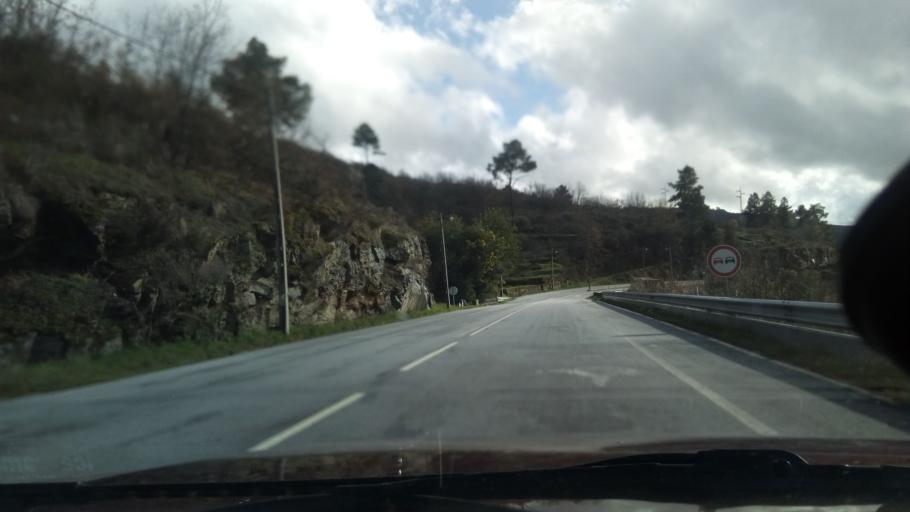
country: PT
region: Guarda
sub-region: Guarda
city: Guarda
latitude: 40.5712
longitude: -7.2972
